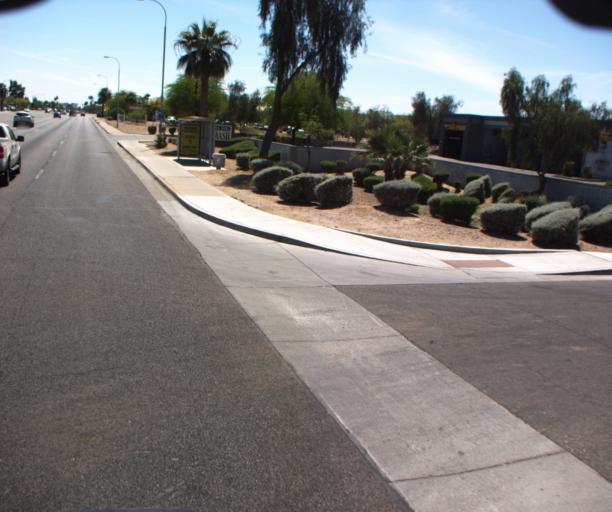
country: US
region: Arizona
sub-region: Maricopa County
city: Chandler
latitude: 33.3247
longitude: -111.8418
